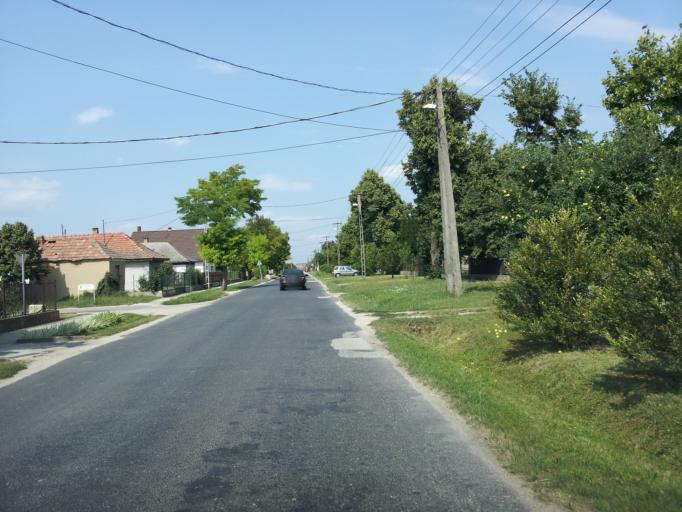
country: HU
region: Veszprem
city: Balatonkenese
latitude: 47.0790
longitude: 18.0777
